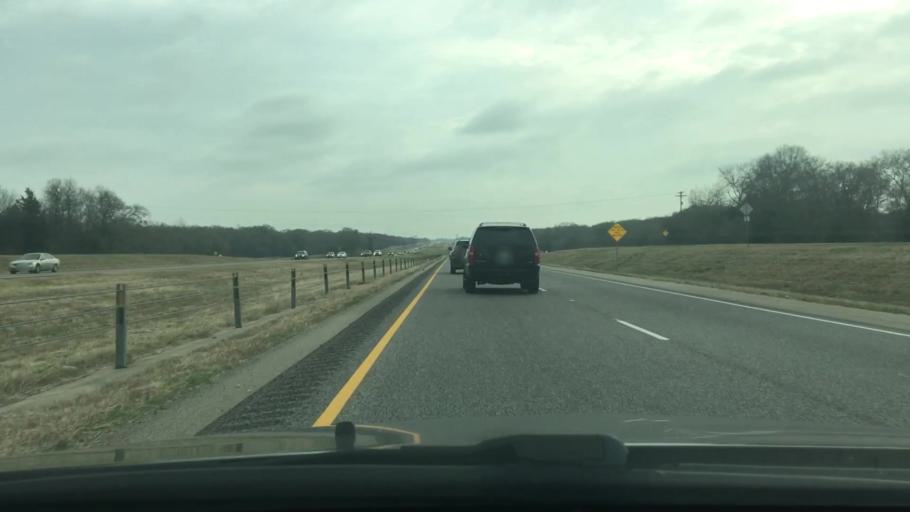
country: US
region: Texas
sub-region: Freestone County
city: Fairfield
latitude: 31.6312
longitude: -96.1580
